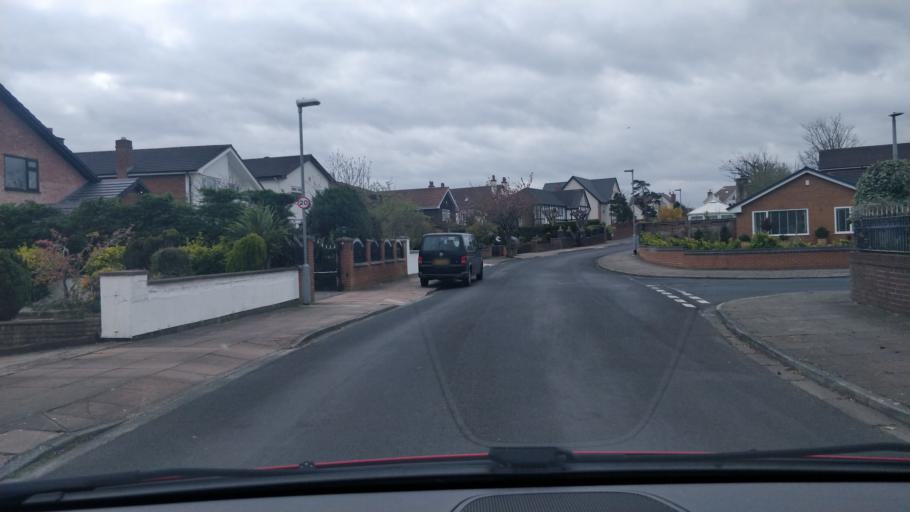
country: GB
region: England
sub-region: Sefton
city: Formby
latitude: 53.6049
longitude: -3.0456
